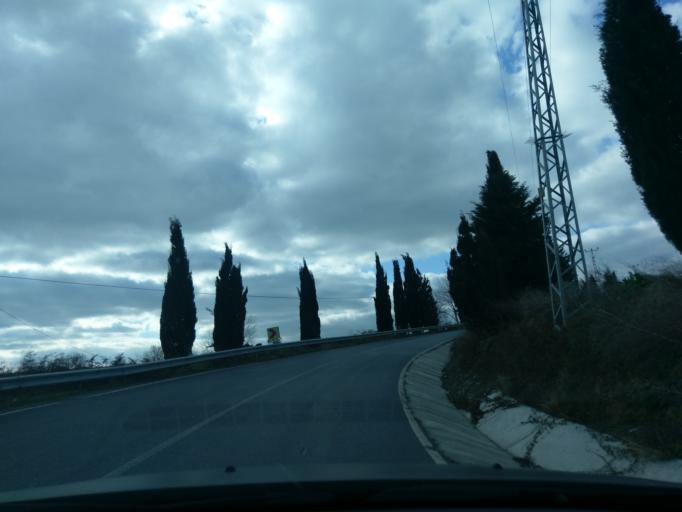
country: TR
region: Istanbul
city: Durusu
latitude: 41.3101
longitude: 28.6939
